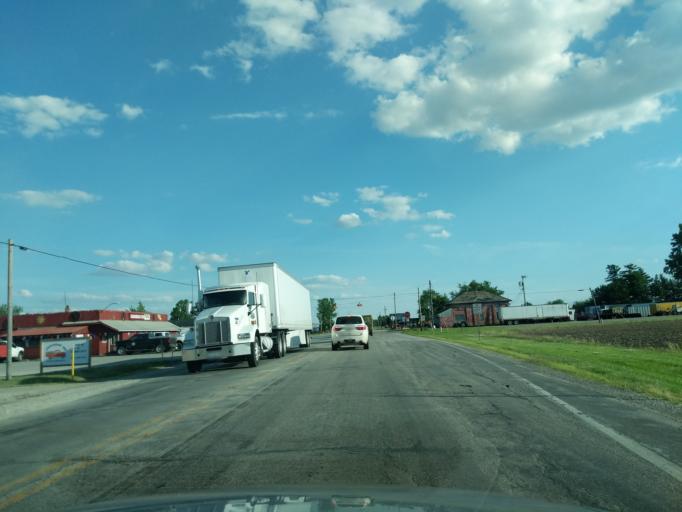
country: US
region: Indiana
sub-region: Whitley County
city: Columbia City
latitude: 41.0785
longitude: -85.4702
